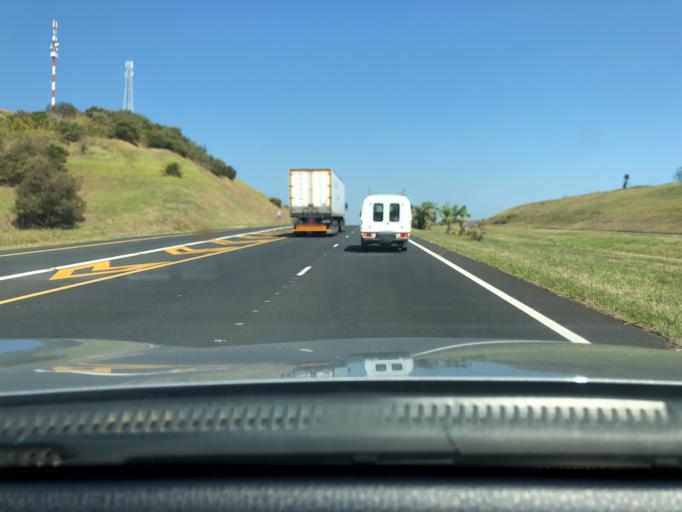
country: ZA
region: KwaZulu-Natal
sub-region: Ugu District Municipality
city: Scottburgh
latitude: -30.2656
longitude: 30.7572
